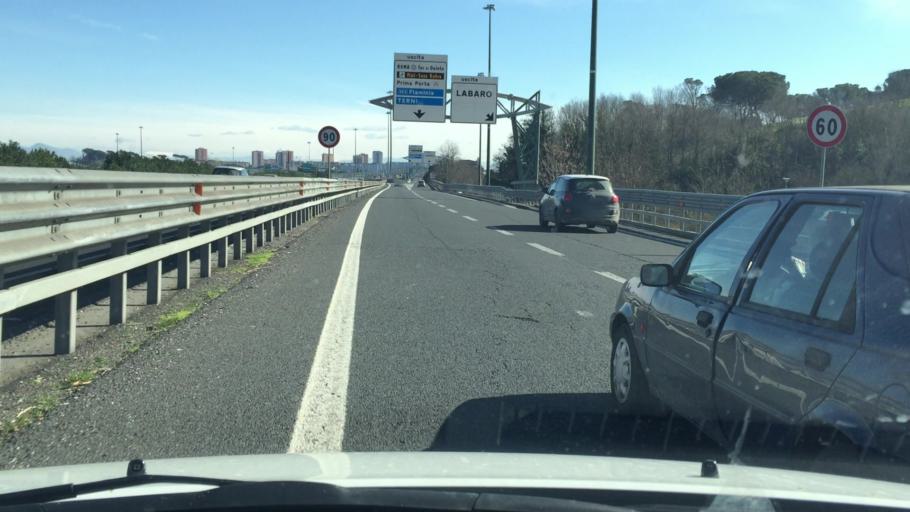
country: IT
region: Latium
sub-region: Citta metropolitana di Roma Capitale
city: Monte Caminetto
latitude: 41.9860
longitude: 12.4848
